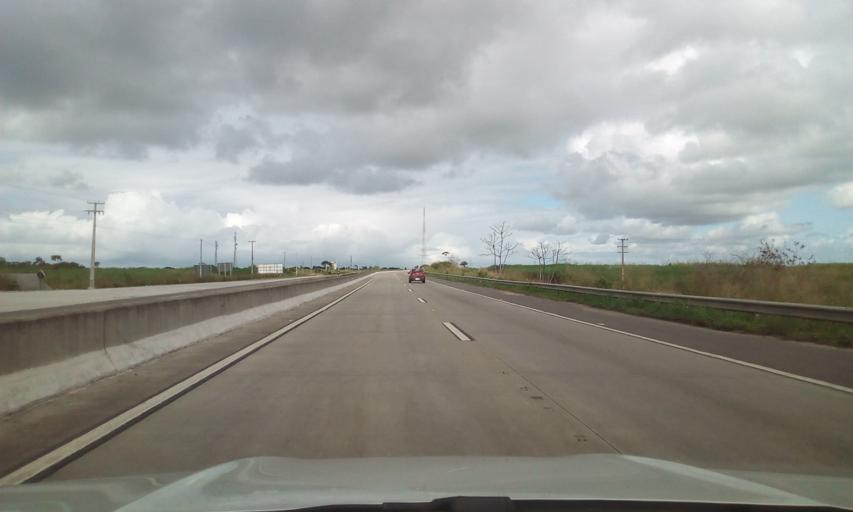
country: BR
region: Pernambuco
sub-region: Goiana
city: Goiana
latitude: -7.6572
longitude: -34.9407
